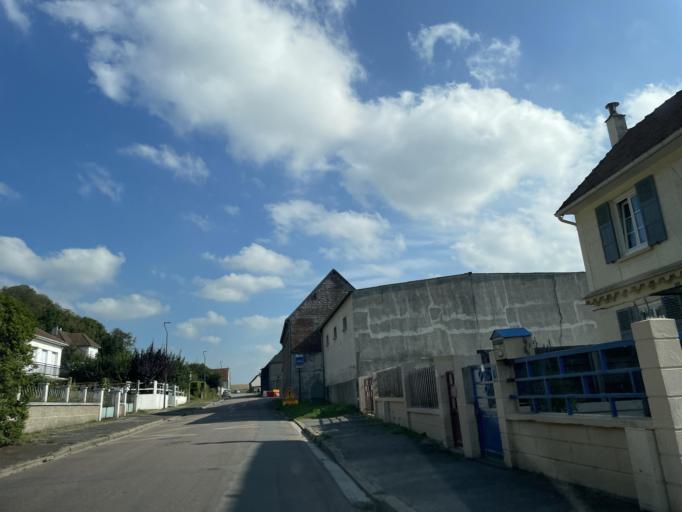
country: FR
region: Haute-Normandie
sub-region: Departement de la Seine-Maritime
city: Criel-sur-Mer
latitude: 50.0390
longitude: 1.3410
